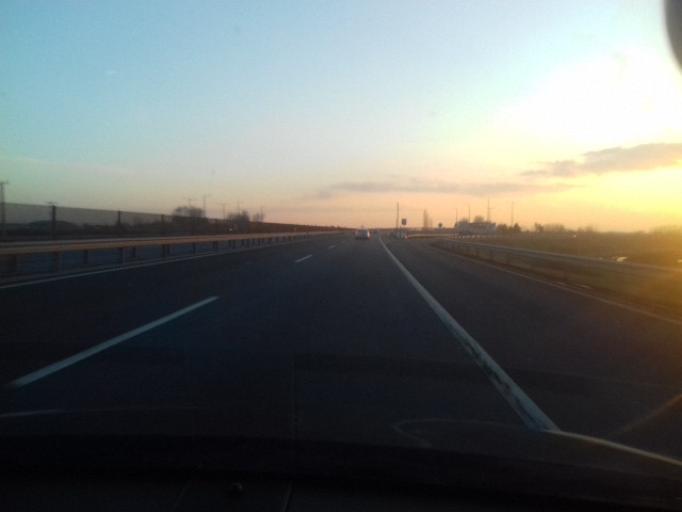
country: HU
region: Hajdu-Bihar
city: Gorbehaza
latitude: 47.8268
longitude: 21.3267
